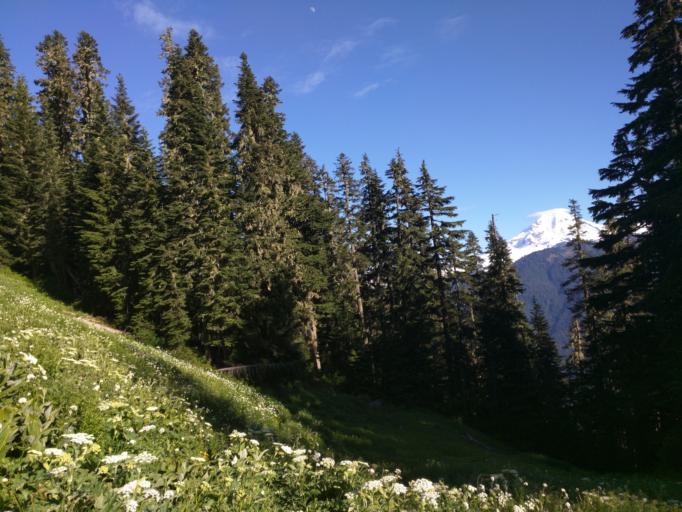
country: CA
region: British Columbia
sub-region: Fraser Valley Regional District
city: Chilliwack
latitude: 48.9266
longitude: -121.8595
